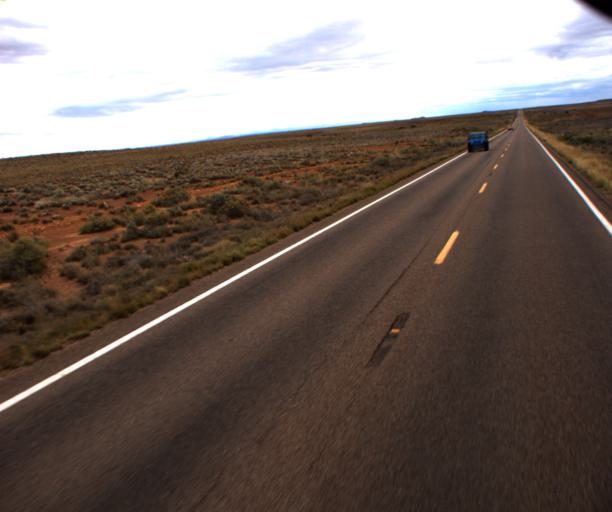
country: US
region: Arizona
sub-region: Navajo County
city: Holbrook
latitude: 34.7809
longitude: -110.1302
